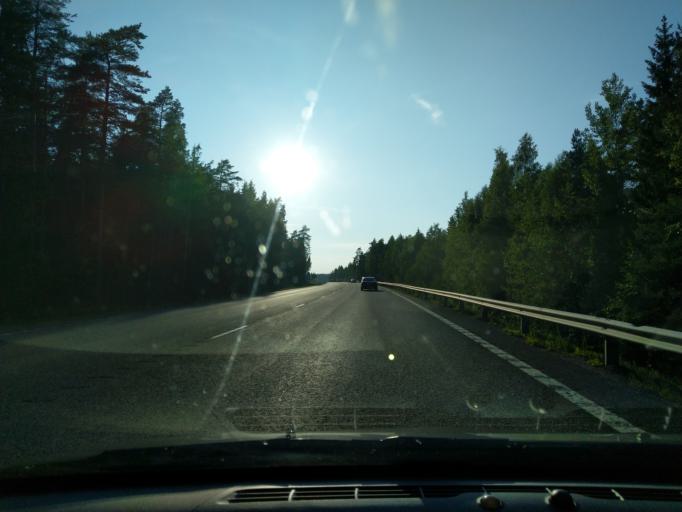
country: FI
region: Paijanne Tavastia
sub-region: Lahti
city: Lahti
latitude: 60.9657
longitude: 25.7423
